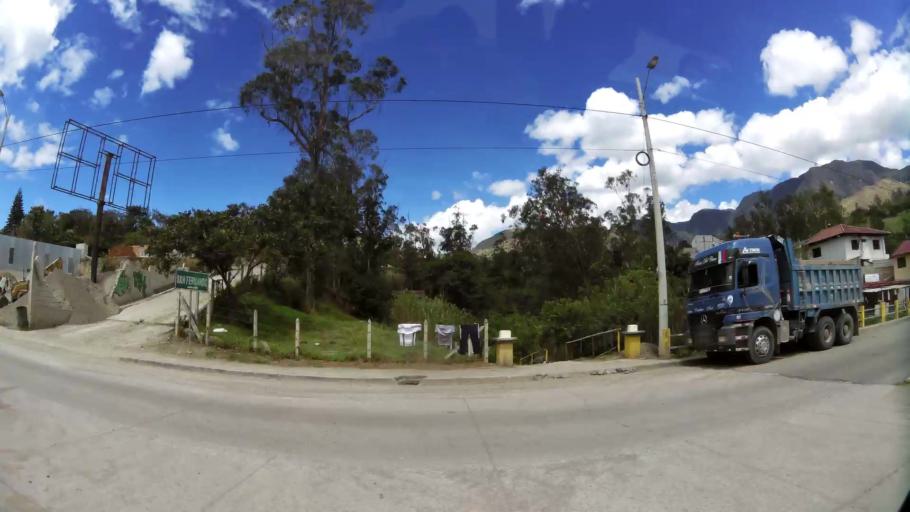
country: EC
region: Azuay
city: Cuenca
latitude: -3.1577
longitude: -79.1486
